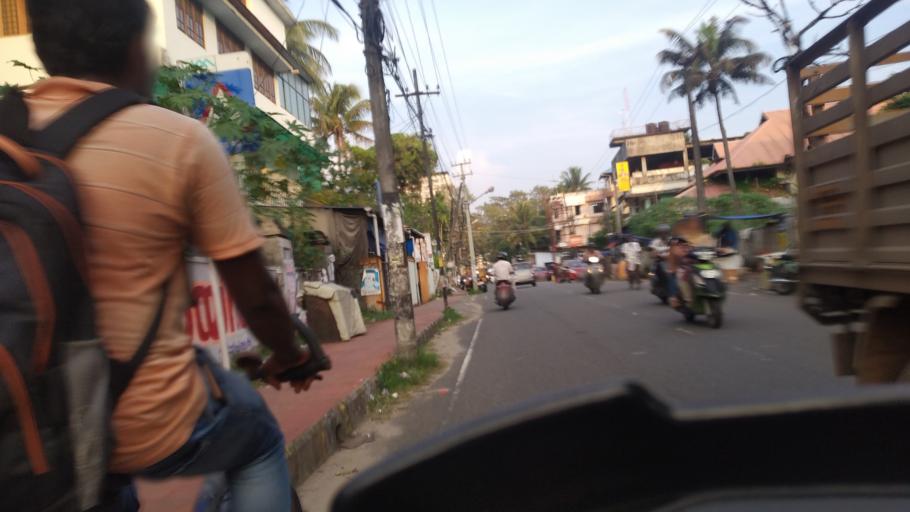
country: IN
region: Kerala
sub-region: Ernakulam
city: Elur
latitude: 10.0191
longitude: 76.2895
